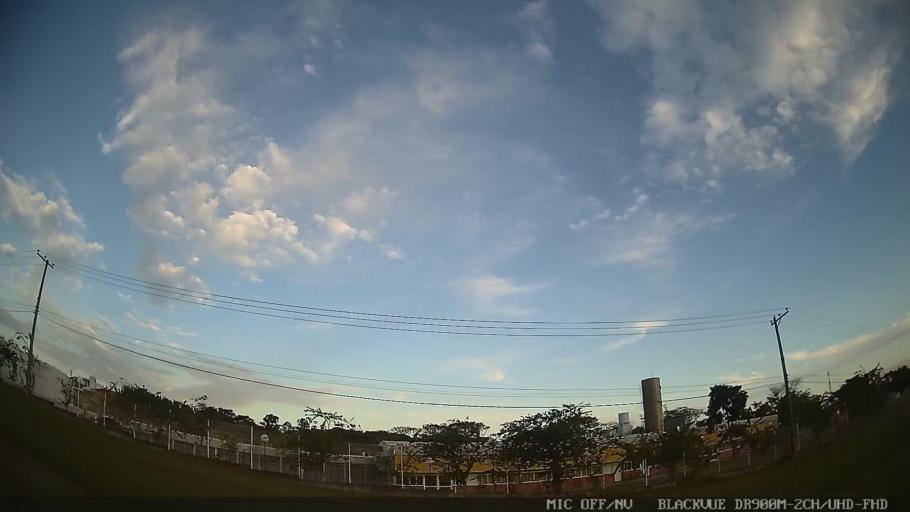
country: BR
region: Sao Paulo
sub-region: Salto
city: Salto
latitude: -23.1792
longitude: -47.2755
